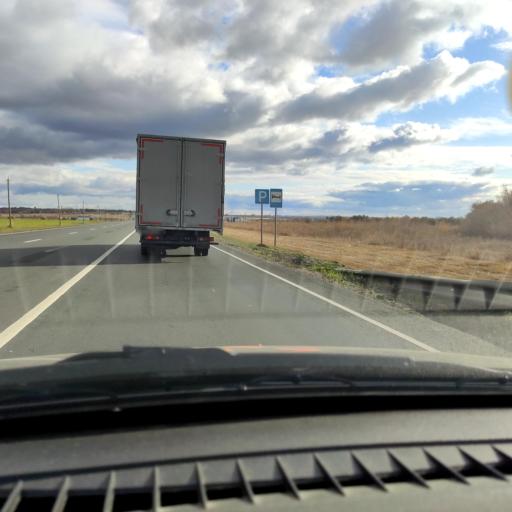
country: RU
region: Samara
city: Syzran'
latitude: 53.2110
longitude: 48.4723
